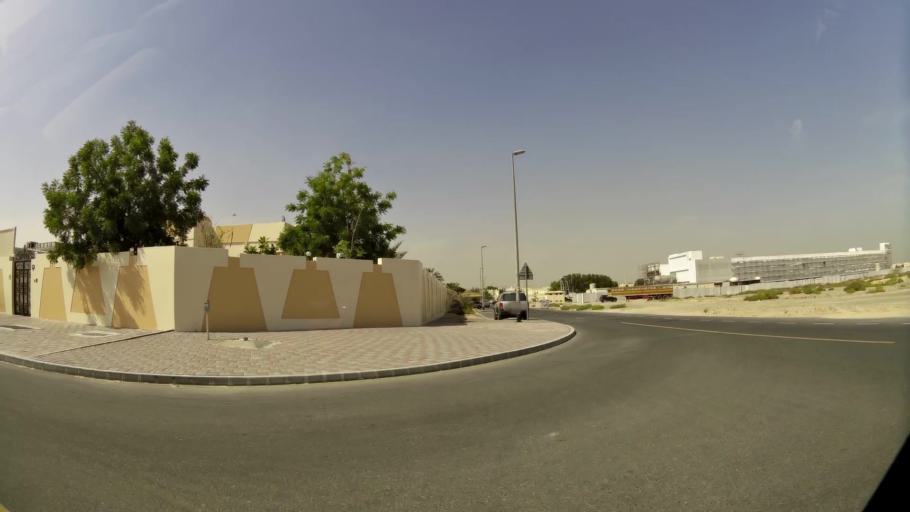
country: AE
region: Ash Shariqah
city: Sharjah
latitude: 25.1998
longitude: 55.4140
